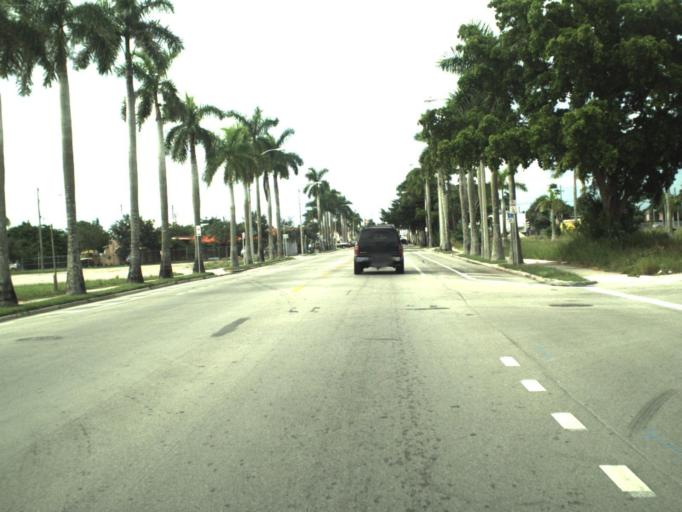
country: US
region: Florida
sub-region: Miami-Dade County
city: Homestead
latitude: 25.4642
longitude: -80.4773
